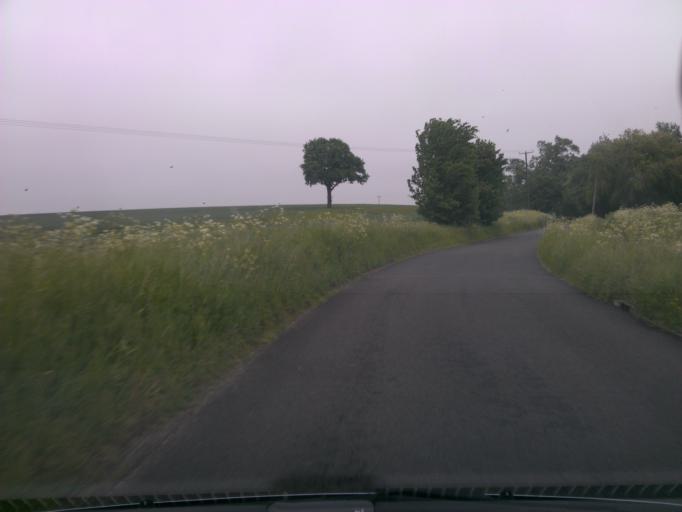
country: GB
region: England
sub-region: Essex
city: Eight Ash Green
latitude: 51.8486
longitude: 0.8063
